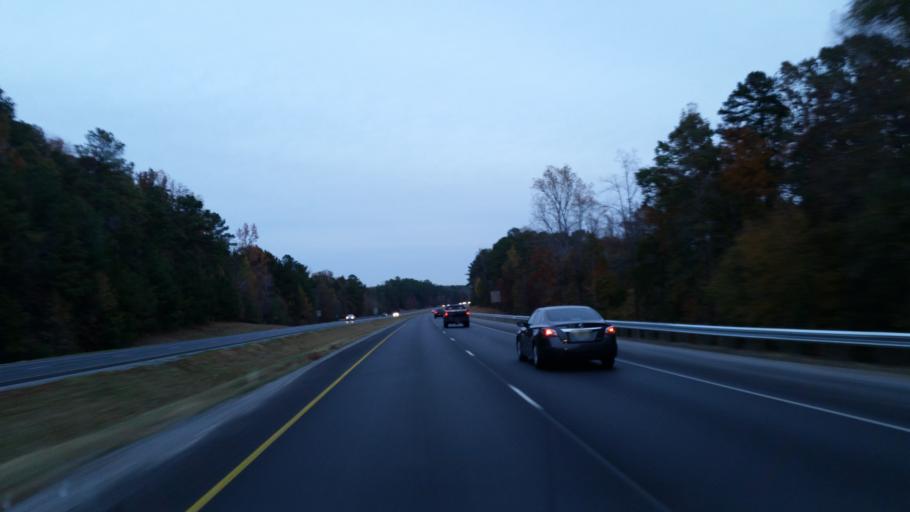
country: US
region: Alabama
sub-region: Greene County
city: Eutaw
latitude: 32.9554
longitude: -87.8339
